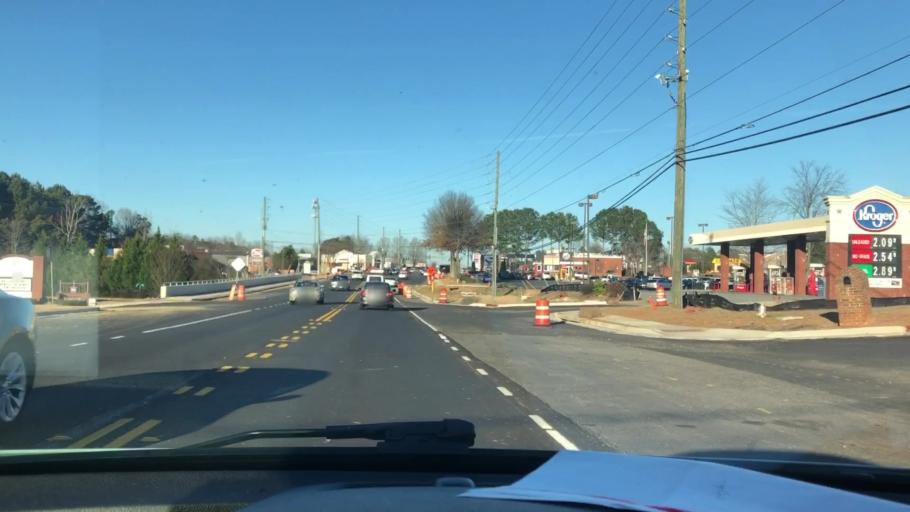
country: US
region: Georgia
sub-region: Gwinnett County
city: Snellville
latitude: 33.8842
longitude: -84.0622
